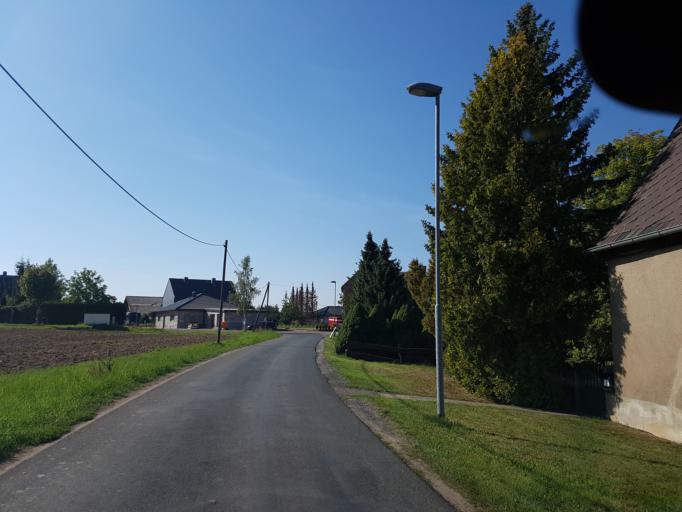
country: DE
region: Saxony
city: Kriebstein
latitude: 51.0582
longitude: 13.0092
